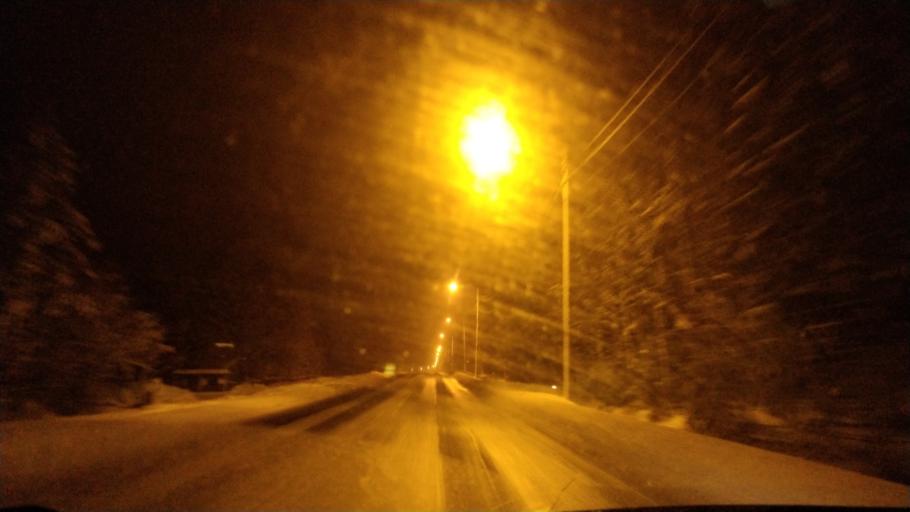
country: FI
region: Lapland
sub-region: Rovaniemi
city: Rovaniemi
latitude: 66.4094
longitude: 25.4015
